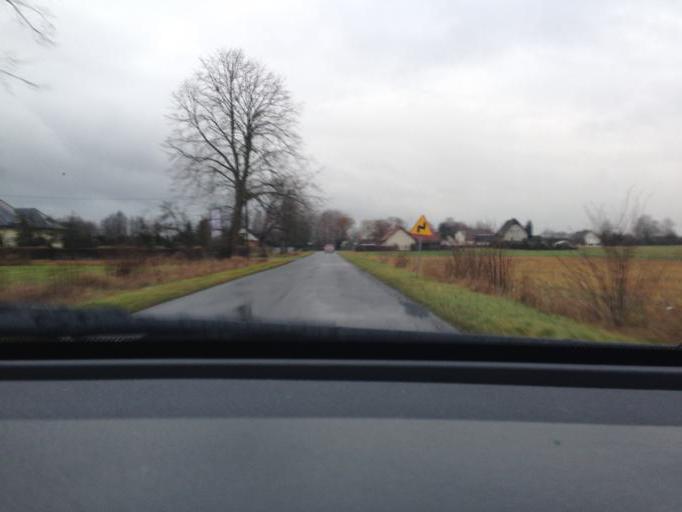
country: PL
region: Opole Voivodeship
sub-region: Powiat opolski
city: Wegry
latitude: 50.7303
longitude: 18.0531
